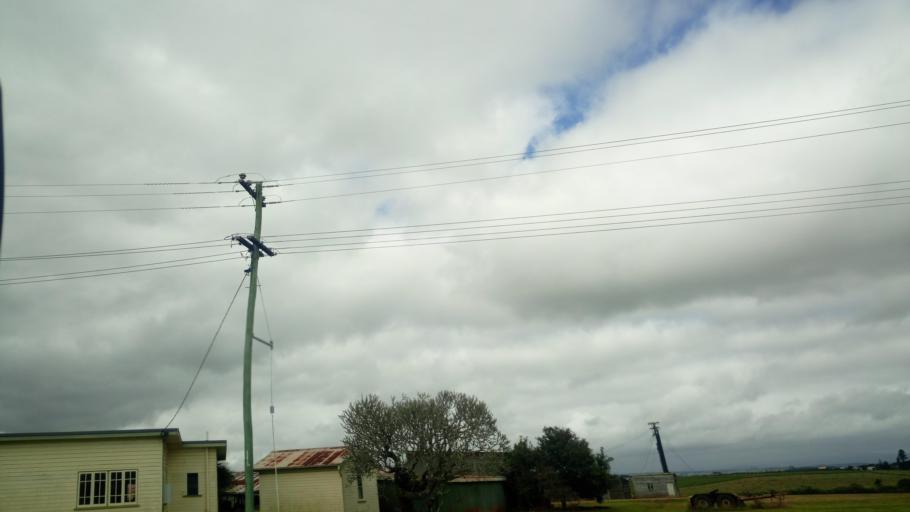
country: AU
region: Queensland
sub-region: Tablelands
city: Tolga
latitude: -17.2165
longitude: 145.5414
